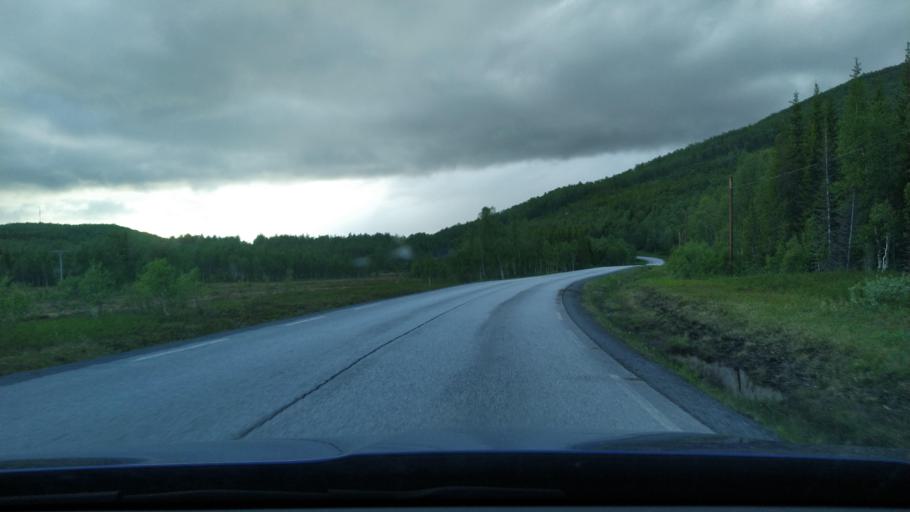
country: NO
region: Troms
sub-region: Dyroy
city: Brostadbotn
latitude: 69.0562
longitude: 17.7855
